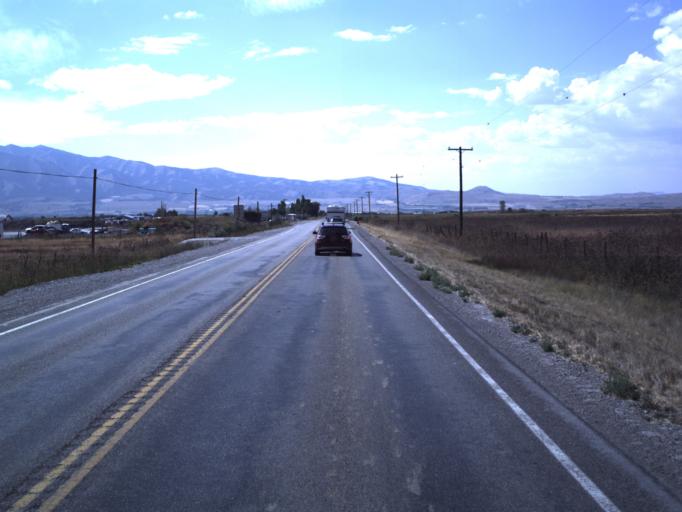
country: US
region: Utah
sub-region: Cache County
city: Logan
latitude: 41.7359
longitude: -111.8756
